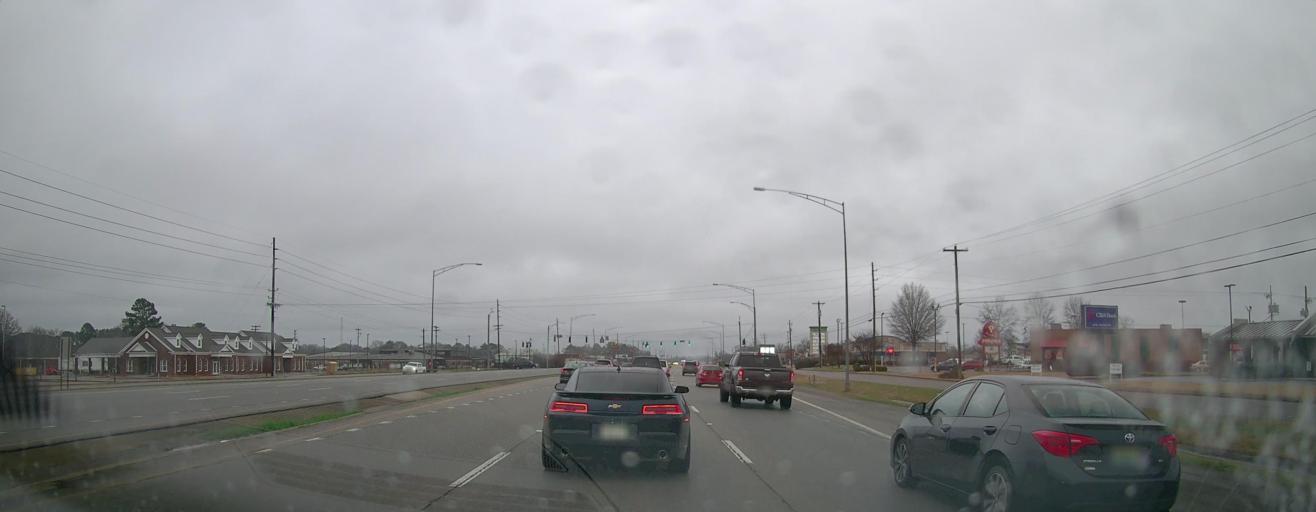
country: US
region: Alabama
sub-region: Morgan County
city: Decatur
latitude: 34.5761
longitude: -87.0173
